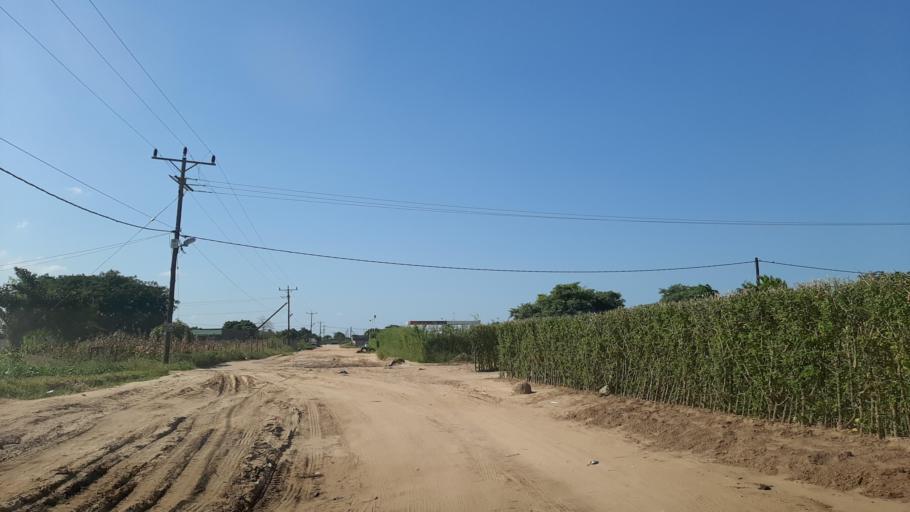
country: MZ
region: Maputo
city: Matola
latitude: -25.8136
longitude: 32.4916
